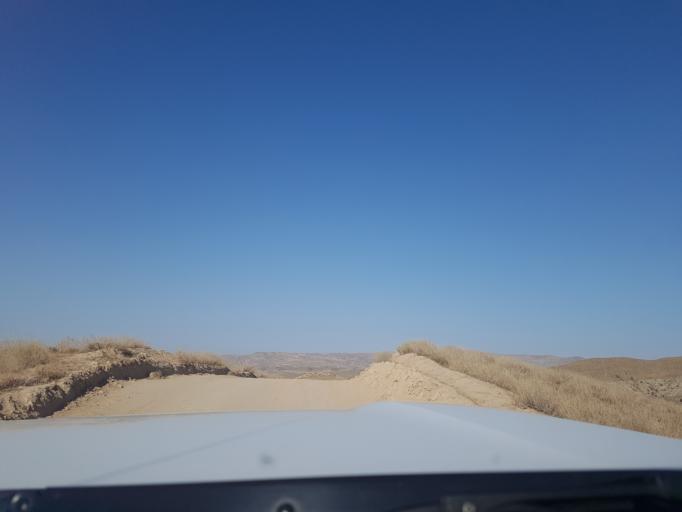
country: TM
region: Balkan
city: Magtymguly
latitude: 38.3037
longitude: 56.8046
